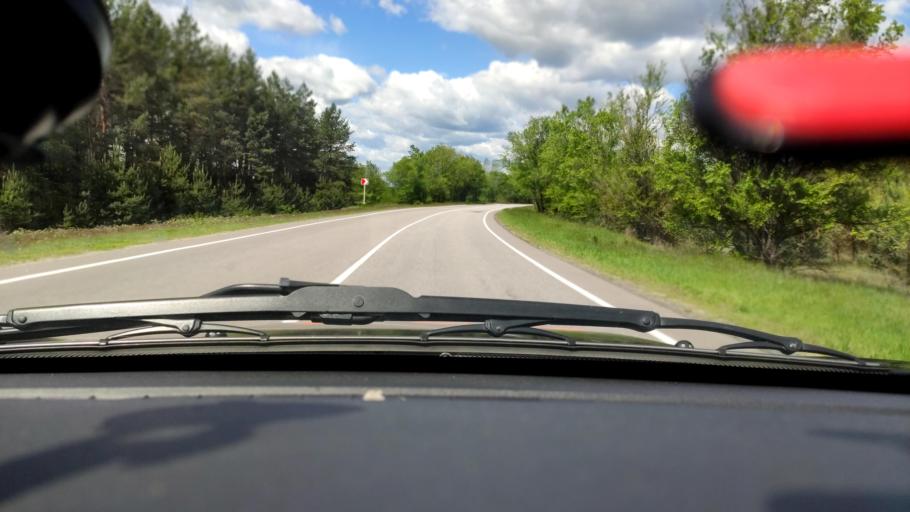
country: RU
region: Voronezj
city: Ostrogozhsk
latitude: 51.0526
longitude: 38.9369
